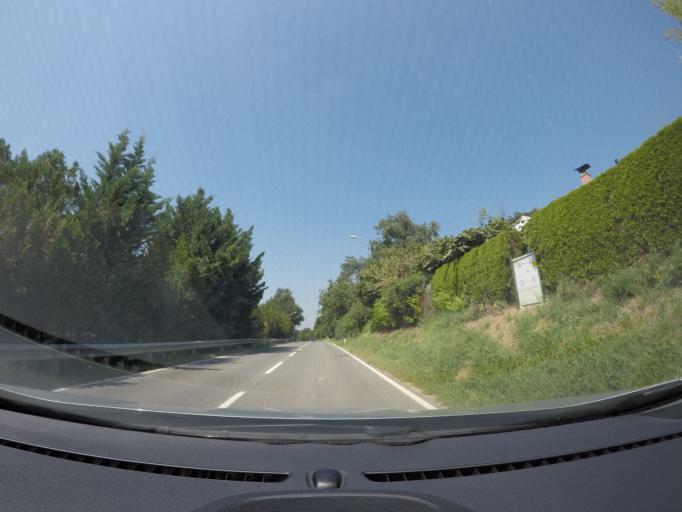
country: AT
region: Lower Austria
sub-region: Politischer Bezirk Sankt Polten
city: Eichgraben
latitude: 48.1776
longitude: 15.9894
